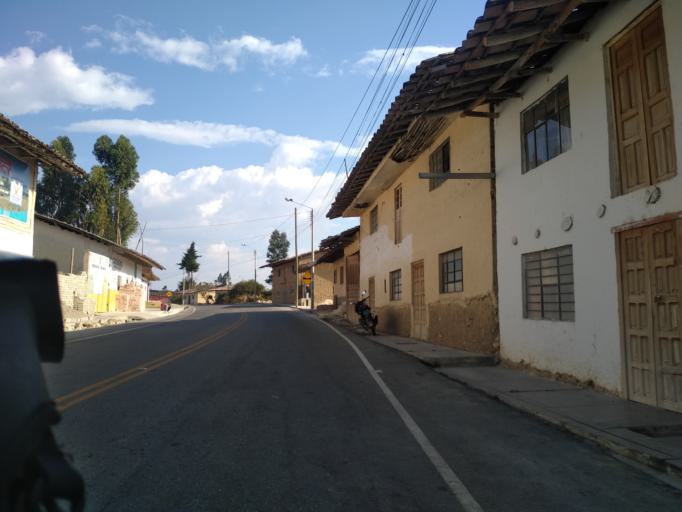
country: PE
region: Cajamarca
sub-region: San Marcos
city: San Marcos
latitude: -7.3842
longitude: -78.1255
